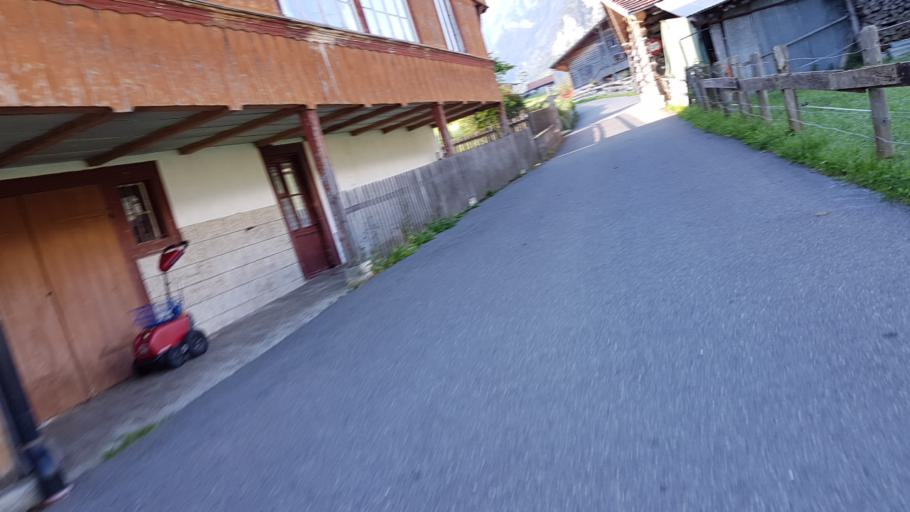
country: CH
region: Bern
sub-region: Frutigen-Niedersimmental District
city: Frutigen
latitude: 46.5799
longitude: 7.6585
